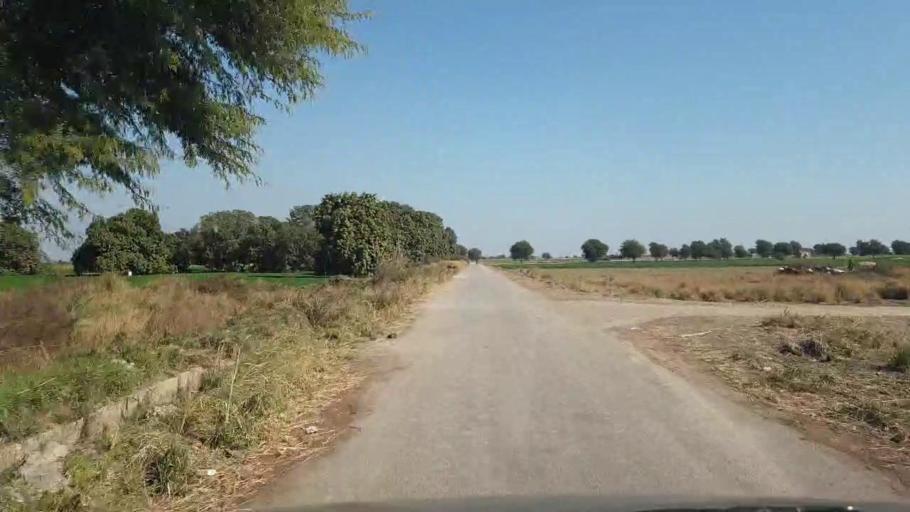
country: PK
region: Sindh
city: Shahpur Chakar
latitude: 26.1079
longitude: 68.6592
